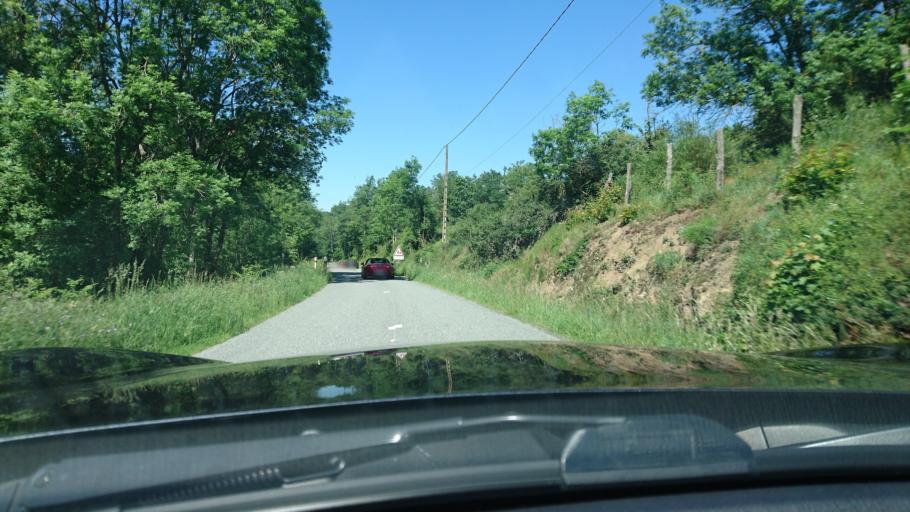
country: FR
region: Rhone-Alpes
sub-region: Departement de la Loire
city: Bussieres
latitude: 45.8812
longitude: 4.2958
